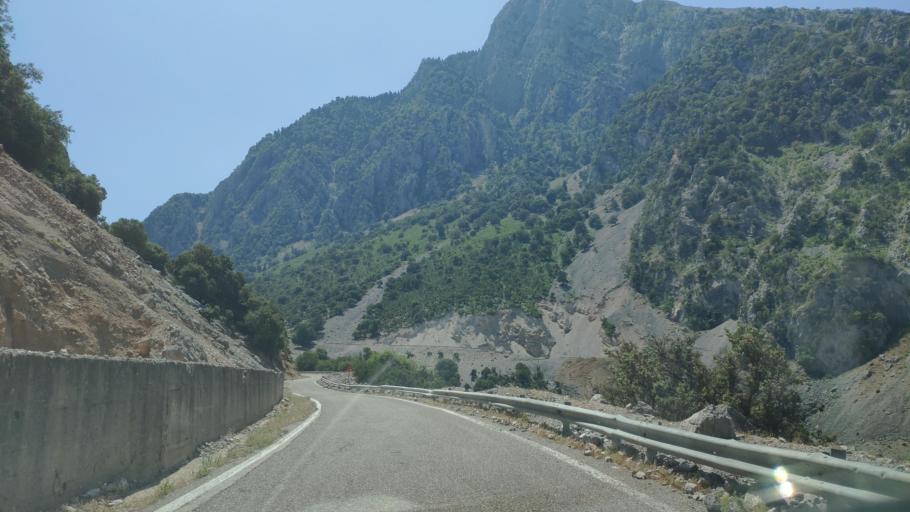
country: GR
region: West Greece
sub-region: Nomos Aitolias kai Akarnanias
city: Krikellos
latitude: 39.0235
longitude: 21.3349
